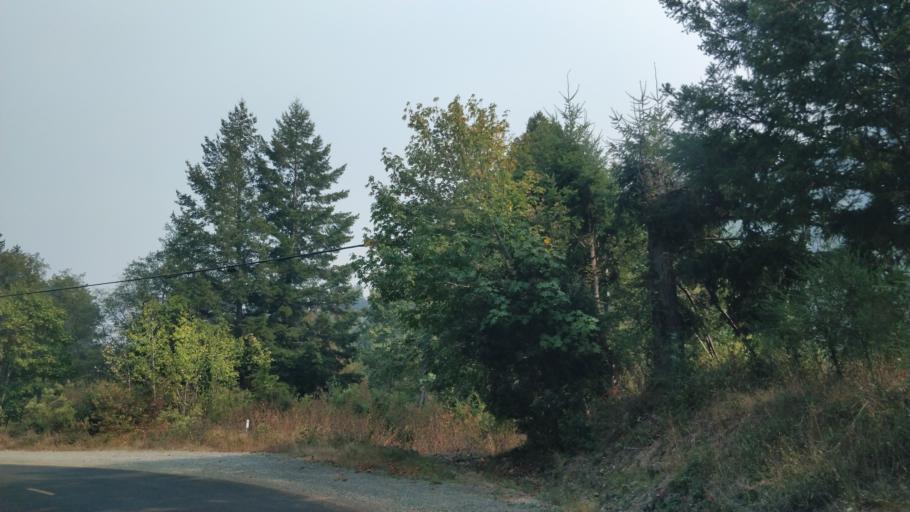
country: US
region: California
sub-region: Humboldt County
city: Rio Dell
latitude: 40.2687
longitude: -124.2284
